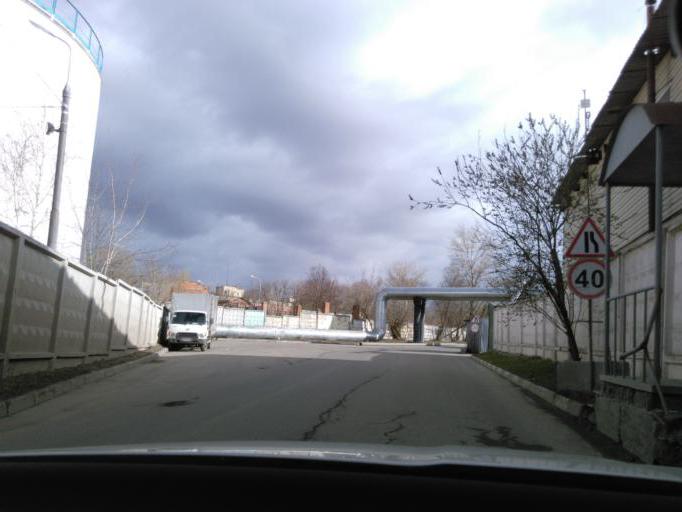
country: RU
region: Moscow
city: Novyye Cheremushki
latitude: 55.6988
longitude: 37.5966
